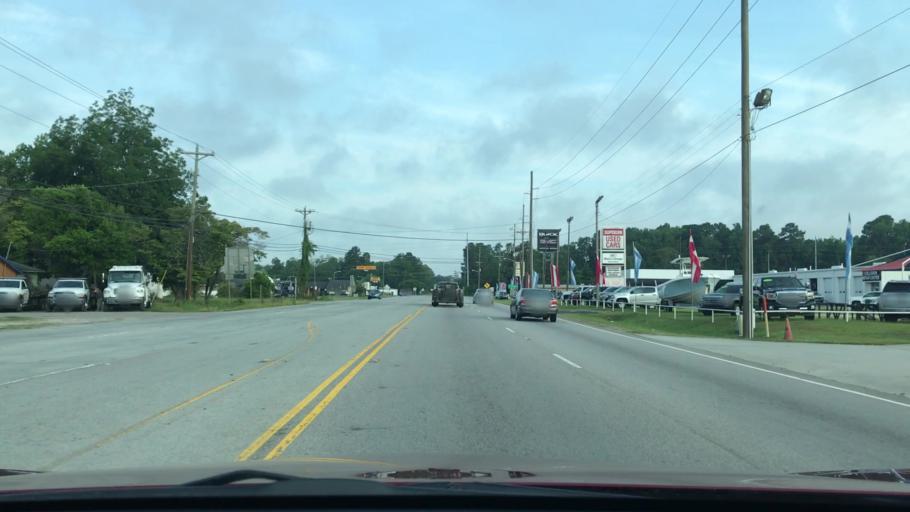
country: US
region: South Carolina
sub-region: Orangeburg County
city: Wilkinson Heights
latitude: 33.4860
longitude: -80.8323
